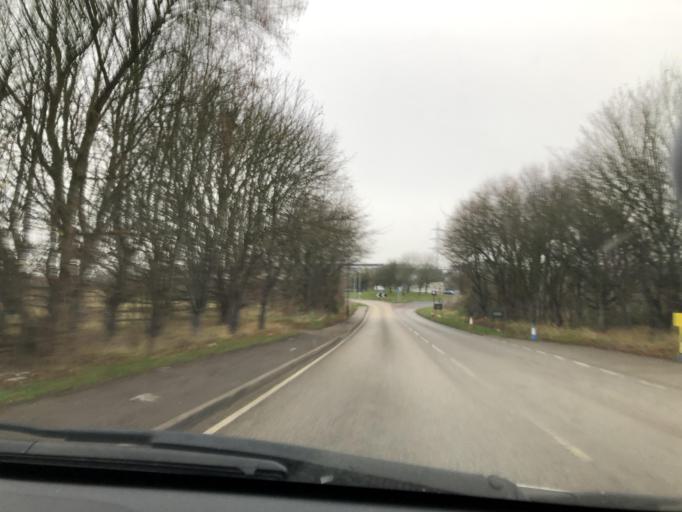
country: GB
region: England
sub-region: Kent
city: Swanscombe
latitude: 51.4237
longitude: 0.3288
